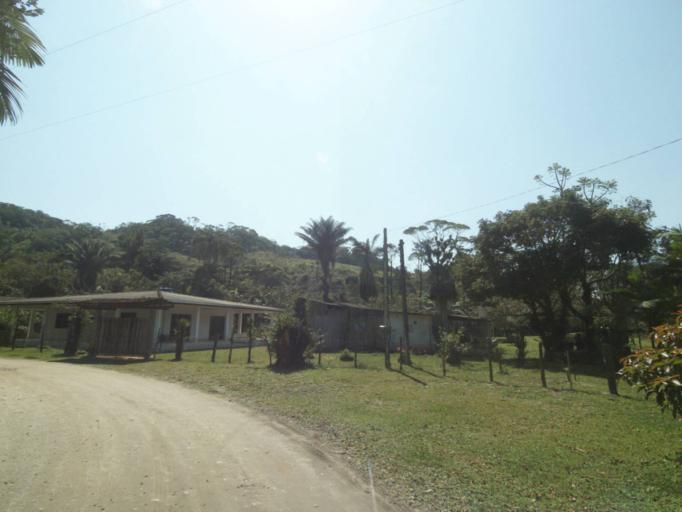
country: BR
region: Parana
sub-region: Paranagua
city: Paranagua
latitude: -25.5492
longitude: -48.5902
